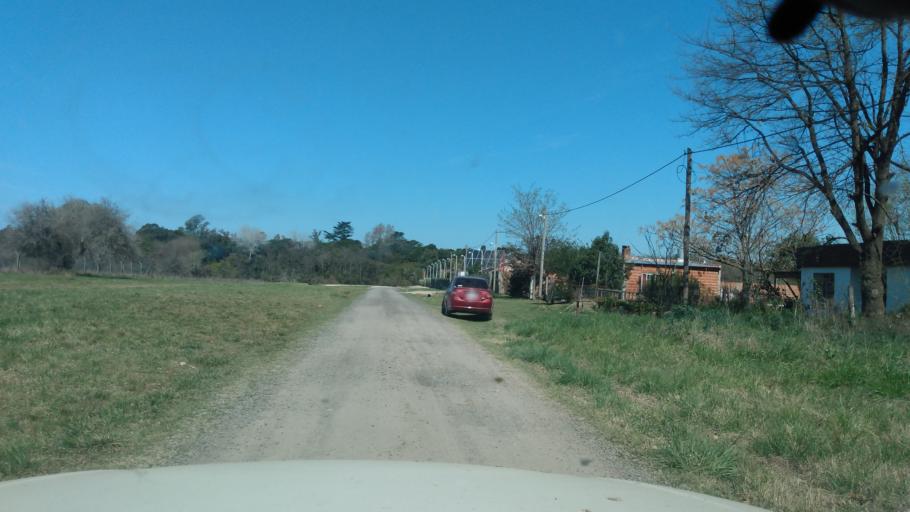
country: AR
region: Buenos Aires
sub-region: Partido de Lujan
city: Lujan
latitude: -34.5752
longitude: -59.1333
